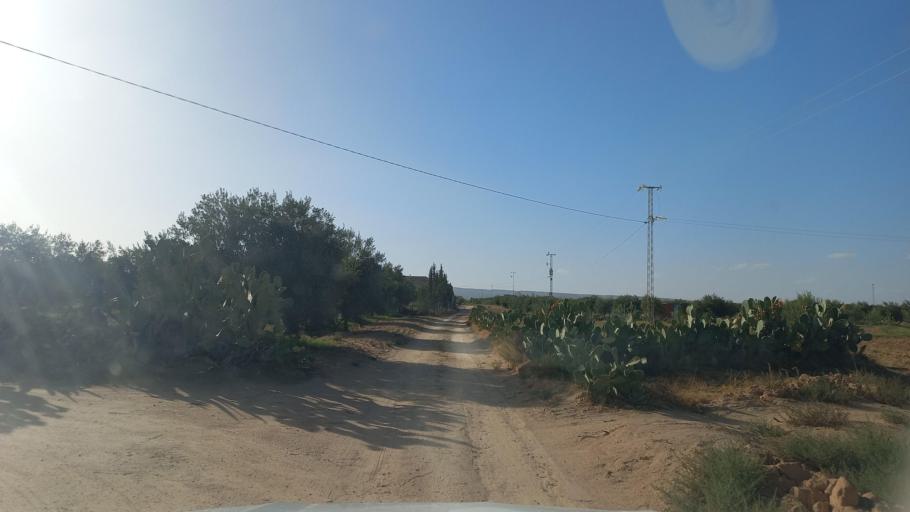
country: TN
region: Al Qasrayn
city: Kasserine
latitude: 35.2636
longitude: 9.0254
